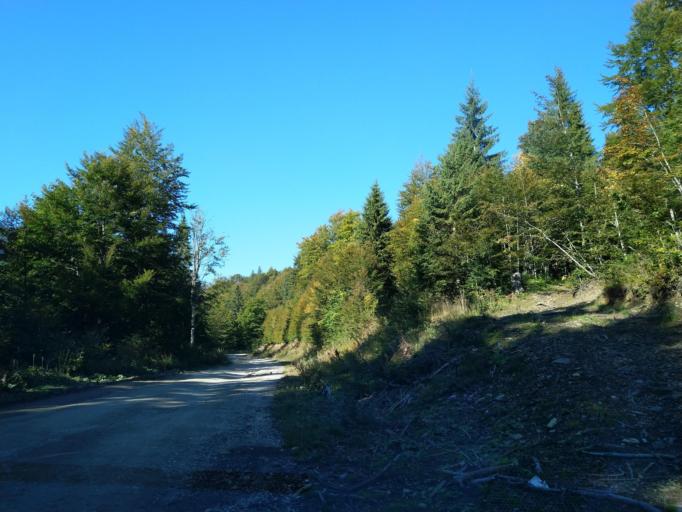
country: RS
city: Sokolovica
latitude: 43.3646
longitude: 20.2588
